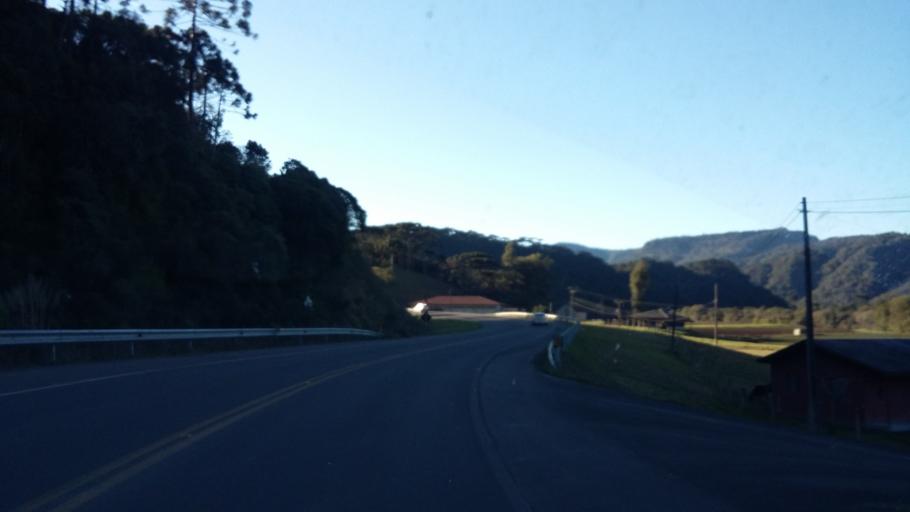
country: BR
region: Santa Catarina
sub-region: Lauro Muller
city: Lauro Muller
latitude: -28.0091
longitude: -49.5356
